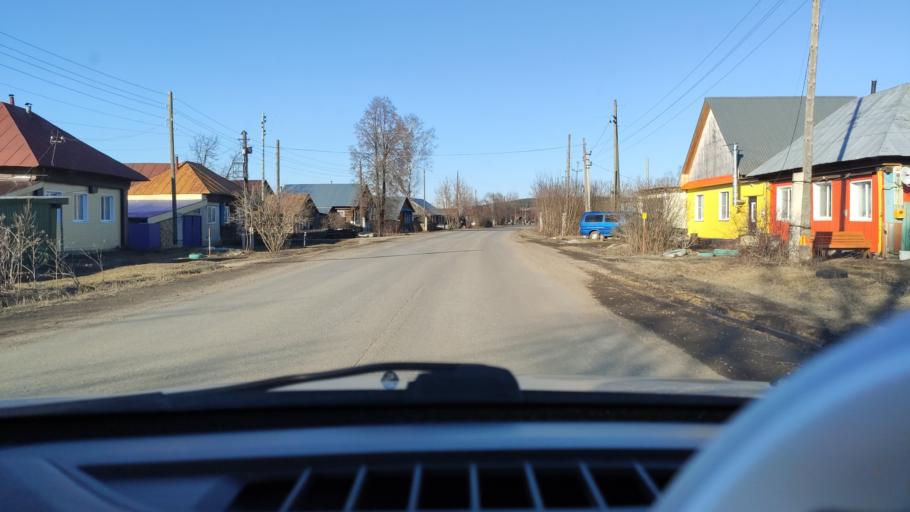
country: RU
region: Perm
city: Suksun
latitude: 57.0302
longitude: 57.4099
